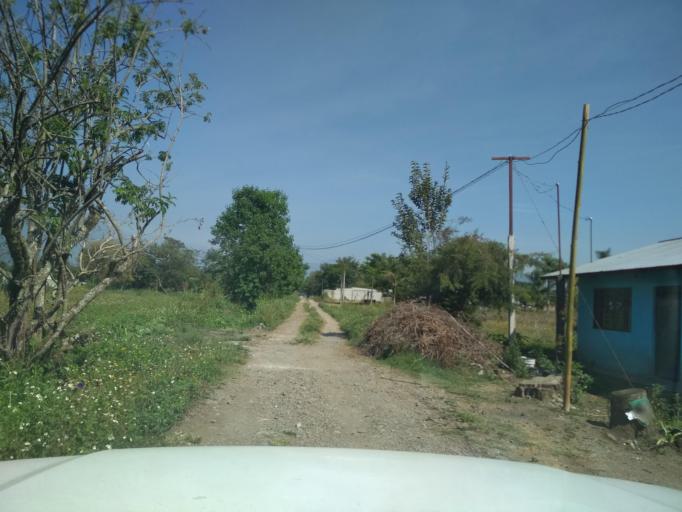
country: MX
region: Veracruz
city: Jalapilla
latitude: 18.8143
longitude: -97.0846
